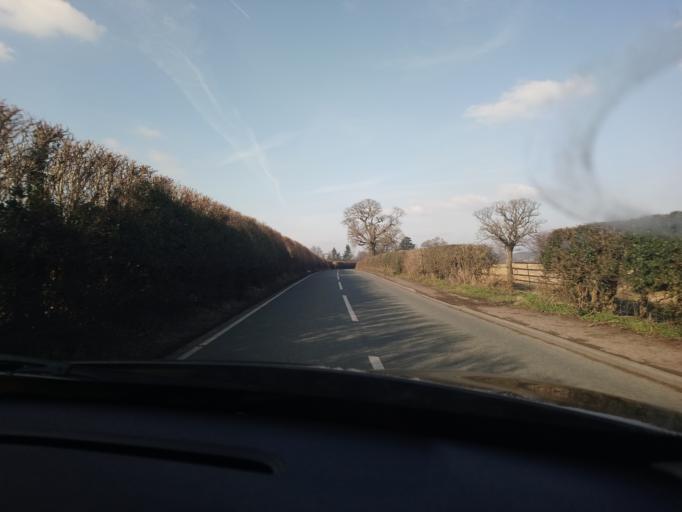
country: GB
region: England
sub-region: Shropshire
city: Bicton
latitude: 52.7489
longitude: -2.7800
